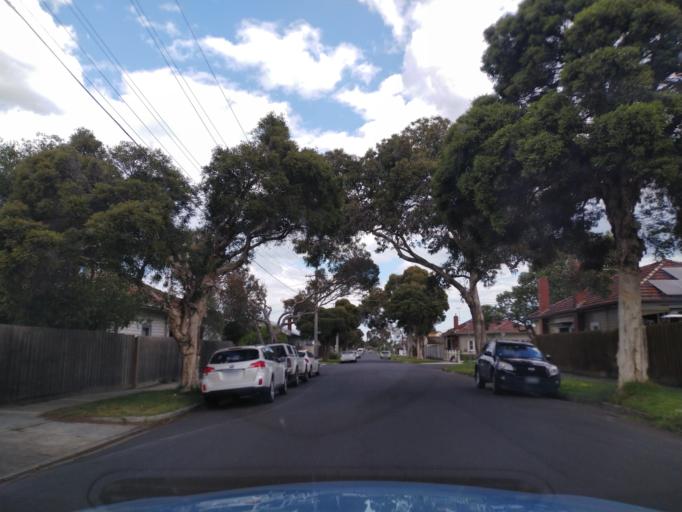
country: AU
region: Victoria
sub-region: Hobsons Bay
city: Newport
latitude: -37.8429
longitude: 144.8768
